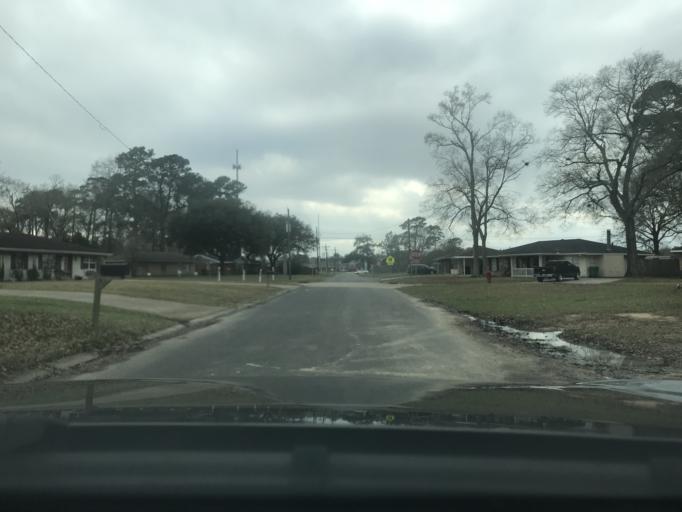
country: US
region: Louisiana
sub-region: Calcasieu Parish
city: Westlake
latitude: 30.2549
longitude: -93.2550
